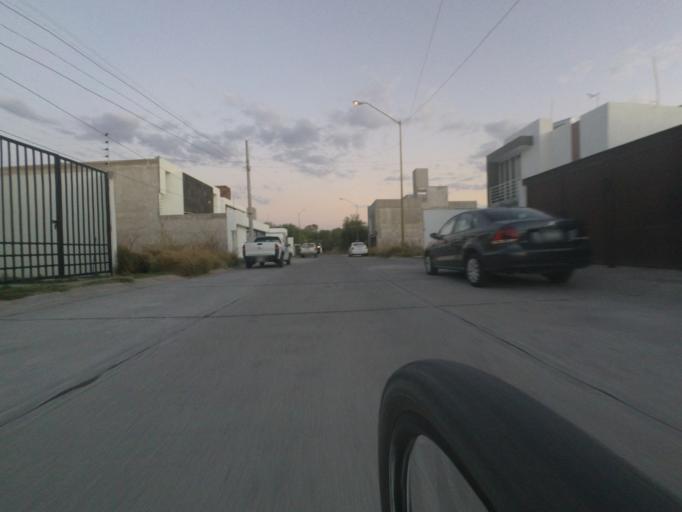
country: MX
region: Aguascalientes
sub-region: Aguascalientes
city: La Loma de los Negritos
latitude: 21.8494
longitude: -102.3305
